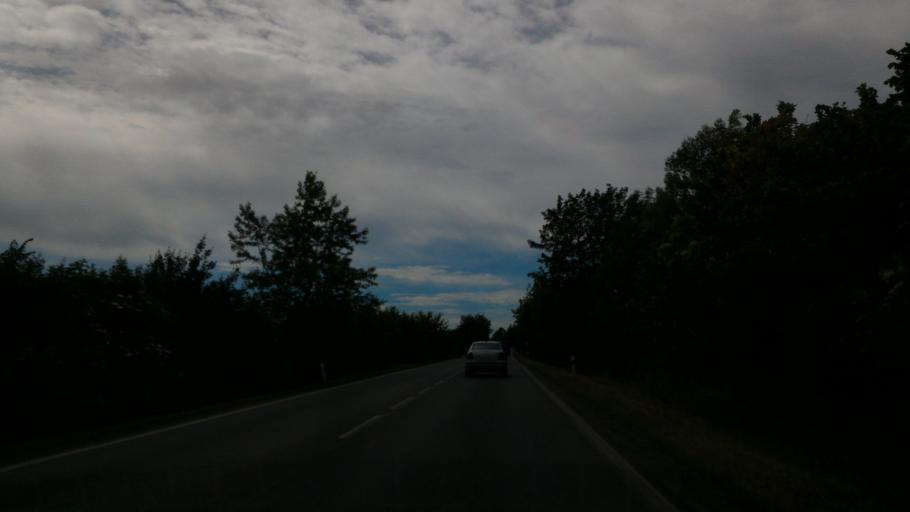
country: CZ
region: Central Bohemia
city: Libeznice
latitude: 50.2218
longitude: 14.4956
